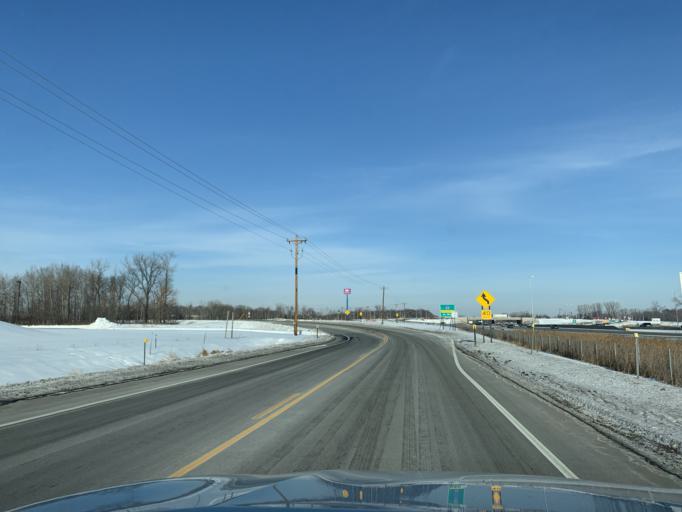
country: US
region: Minnesota
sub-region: Anoka County
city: Columbus
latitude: 45.2462
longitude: -93.0274
